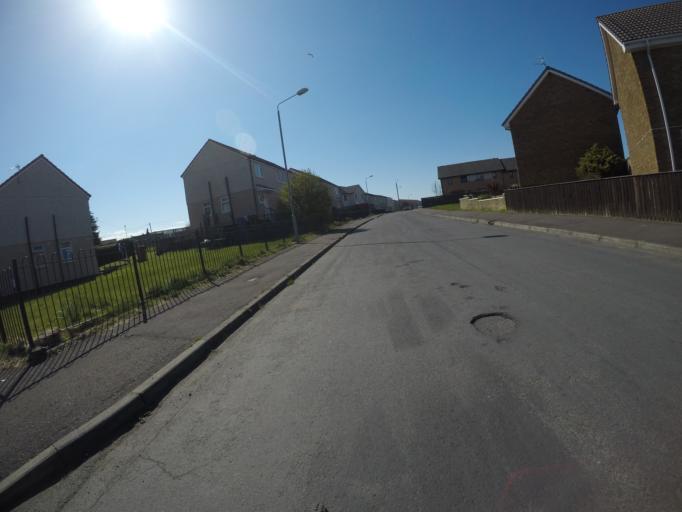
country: GB
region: Scotland
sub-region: North Ayrshire
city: Irvine
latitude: 55.6228
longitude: -4.6636
